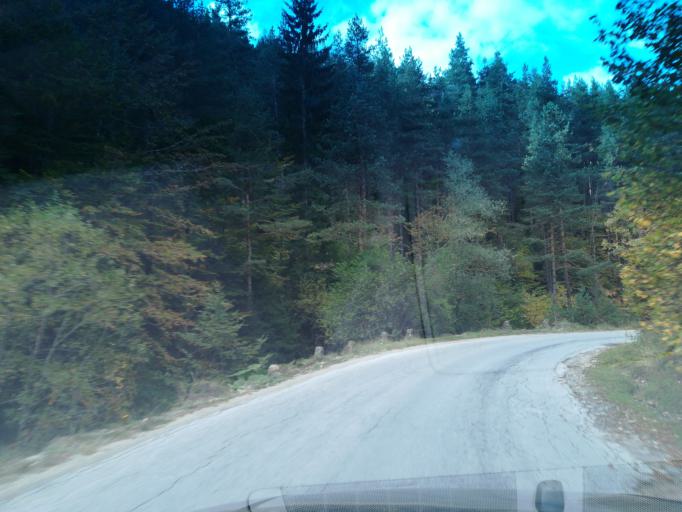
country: BG
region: Pazardzhik
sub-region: Obshtina Batak
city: Batak
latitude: 41.9451
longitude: 24.2472
